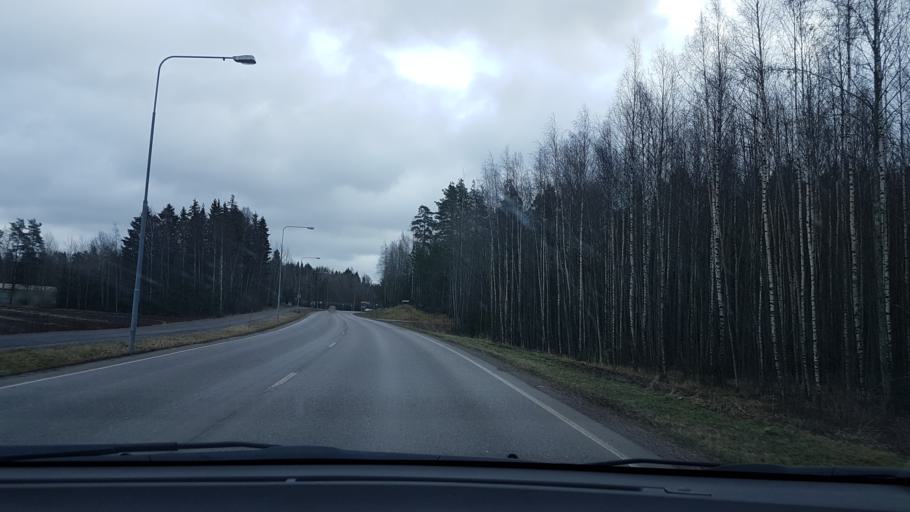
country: FI
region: Uusimaa
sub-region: Helsinki
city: Kerava
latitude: 60.3714
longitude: 25.0657
